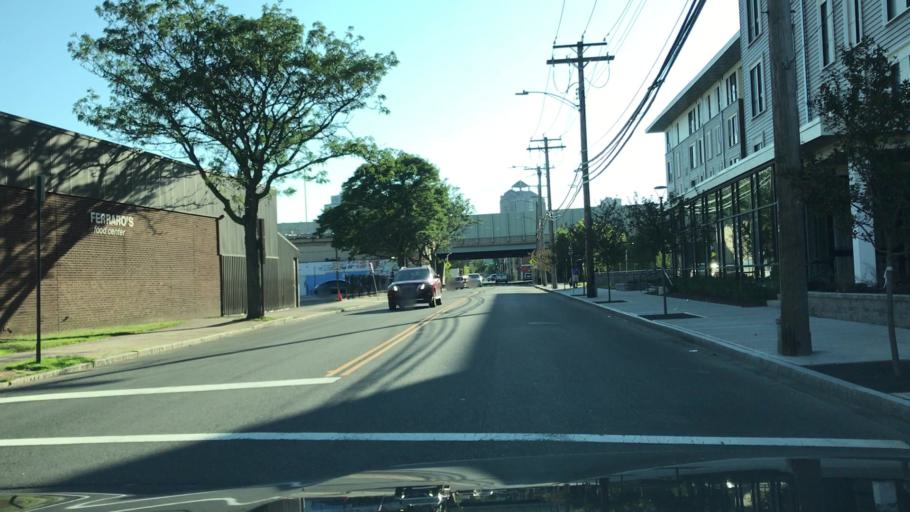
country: US
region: Connecticut
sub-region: New Haven County
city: New Haven
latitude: 41.3085
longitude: -72.9125
